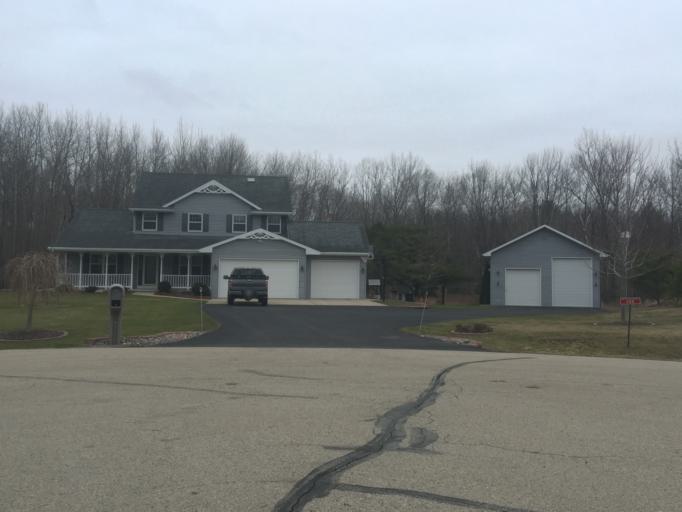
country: US
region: Wisconsin
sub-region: Brown County
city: Suamico
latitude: 44.6910
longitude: -88.0647
